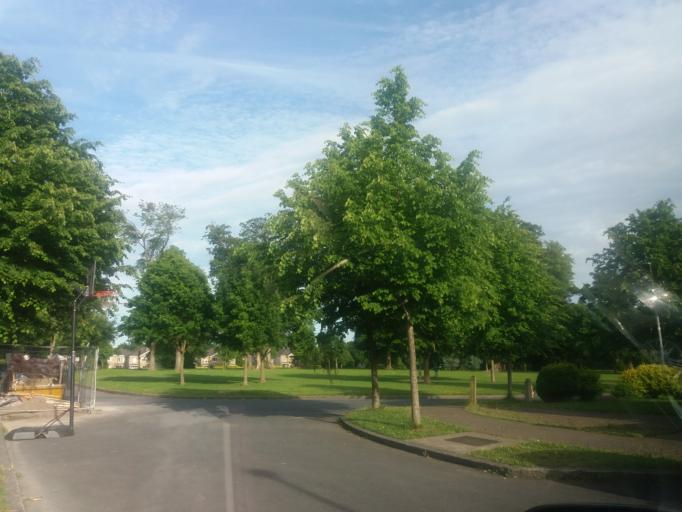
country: IE
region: Leinster
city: Hartstown
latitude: 53.3848
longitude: -6.4151
